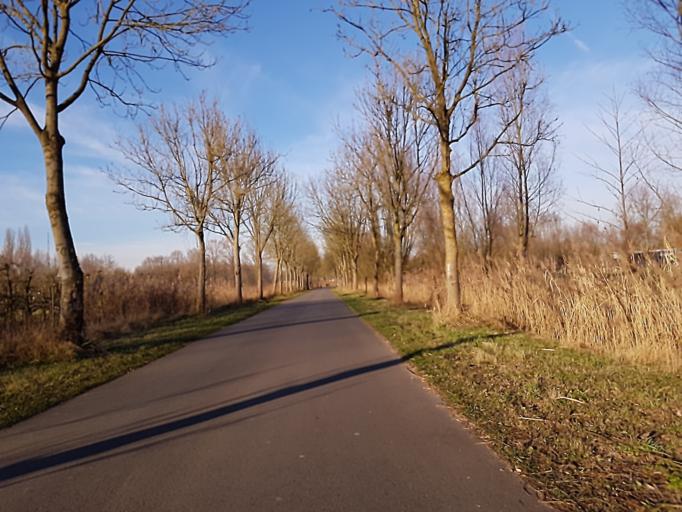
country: BE
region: Flanders
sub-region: Provincie Antwerpen
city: Puurs
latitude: 51.1102
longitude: 4.2863
